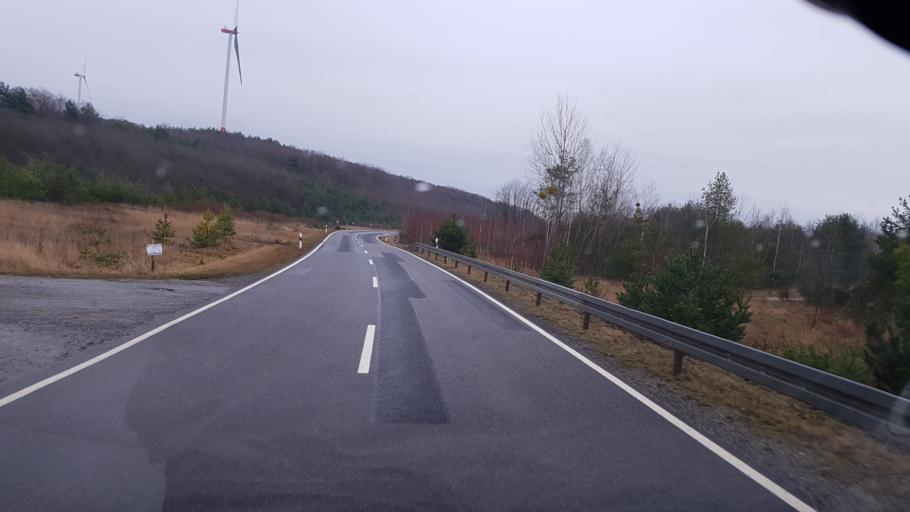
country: DE
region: Brandenburg
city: Schwarzheide
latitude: 51.5118
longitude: 13.8473
